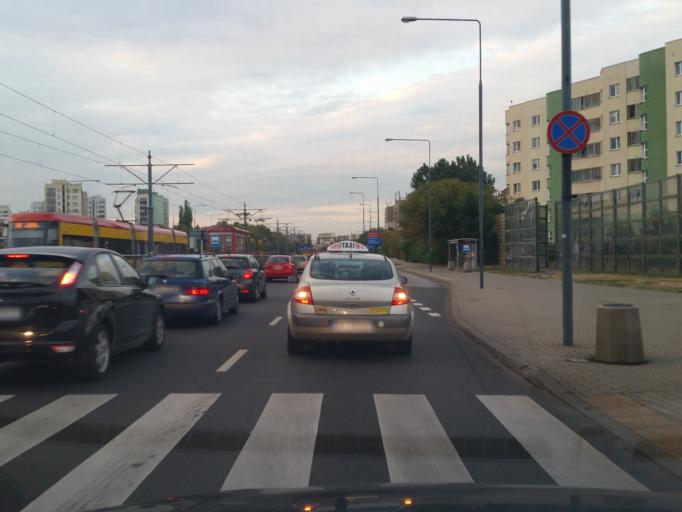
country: PL
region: Masovian Voivodeship
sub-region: Warszawa
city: Bielany
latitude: 52.2687
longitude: 20.9328
